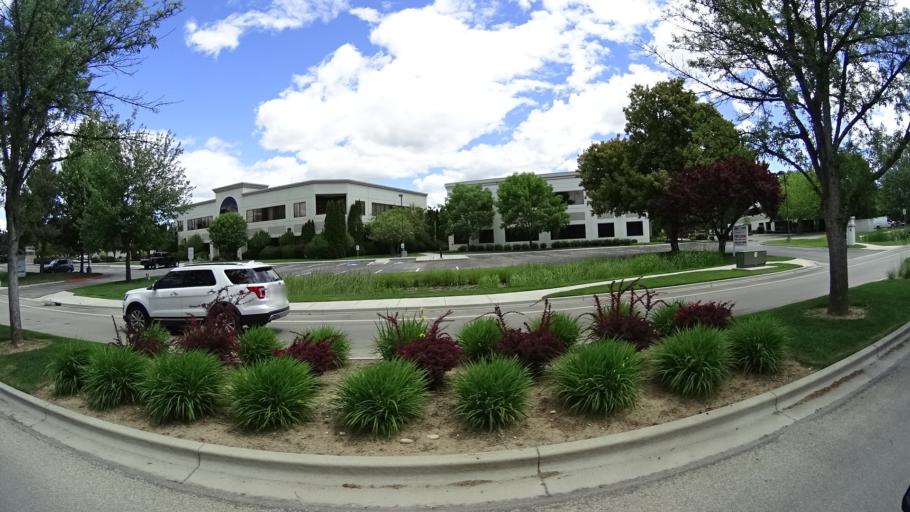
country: US
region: Idaho
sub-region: Ada County
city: Eagle
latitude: 43.6608
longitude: -116.3390
